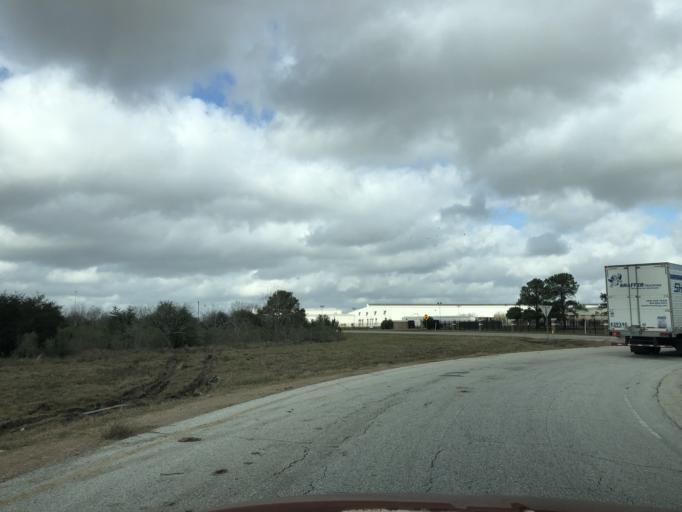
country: US
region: Texas
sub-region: Austin County
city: Sealy
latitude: 29.7596
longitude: -96.2189
